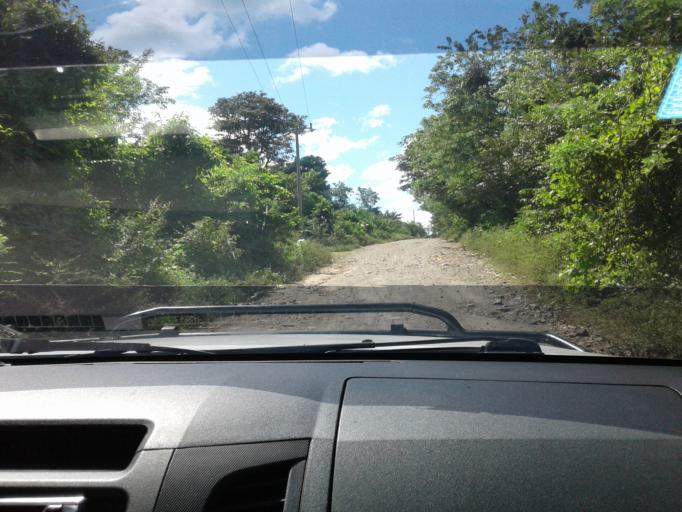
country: NI
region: Rivas
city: Altagracia
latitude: 11.4773
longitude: -85.5529
